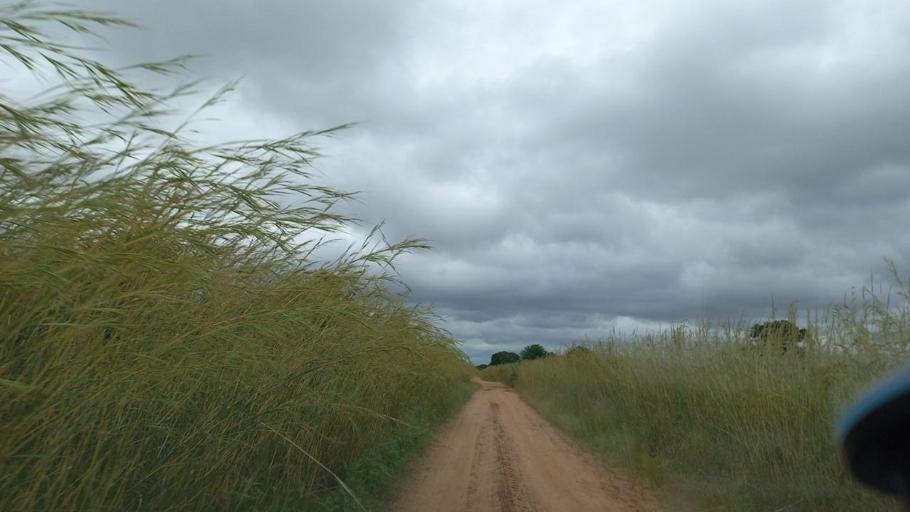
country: ZM
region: Lusaka
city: Lusaka
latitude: -15.1251
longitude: 28.3709
